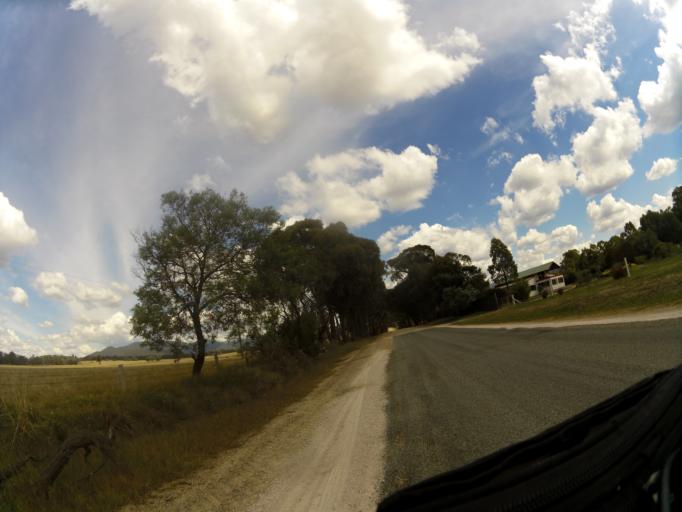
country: AU
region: Victoria
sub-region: Benalla
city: Benalla
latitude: -36.7483
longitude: 145.9859
